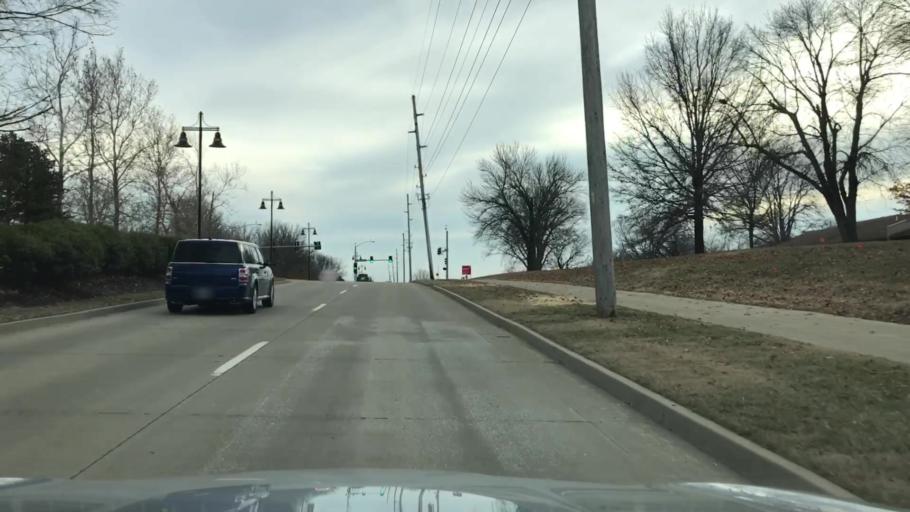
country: US
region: Missouri
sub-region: Jackson County
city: Lees Summit
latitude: 38.9214
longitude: -94.4131
